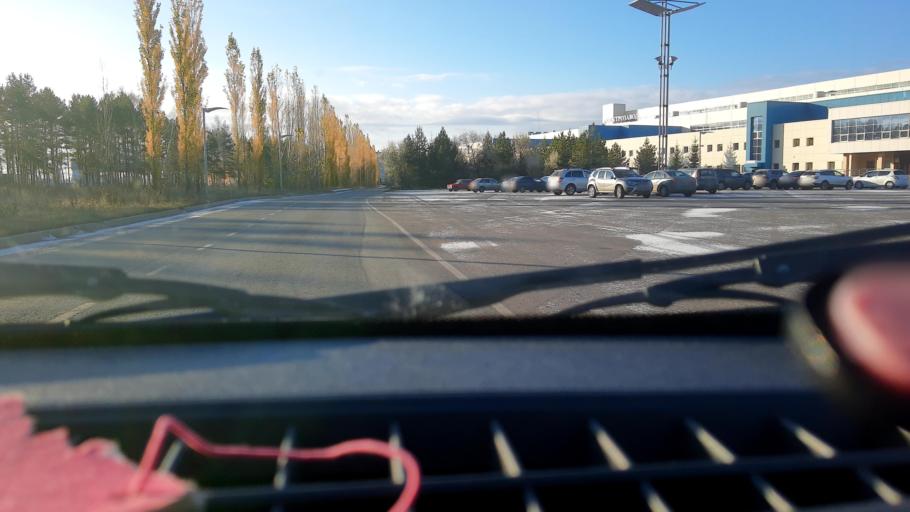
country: RU
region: Bashkortostan
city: Ufa
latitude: 54.5904
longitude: 55.9103
